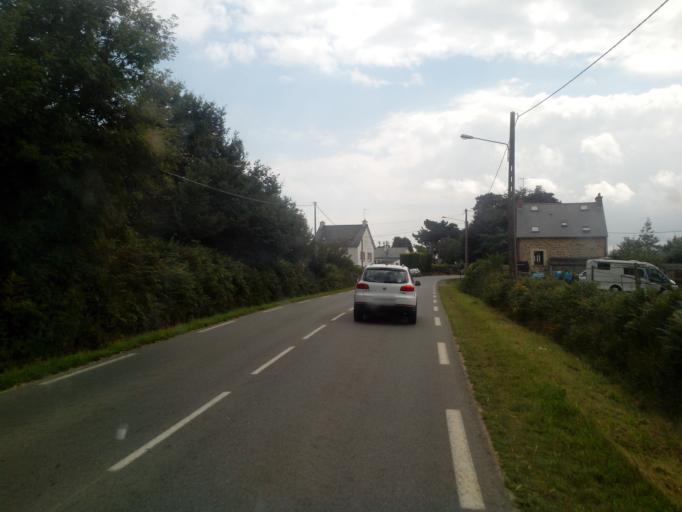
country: FR
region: Brittany
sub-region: Departement des Cotes-d'Armor
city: Plouha
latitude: 48.6984
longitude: -2.9416
